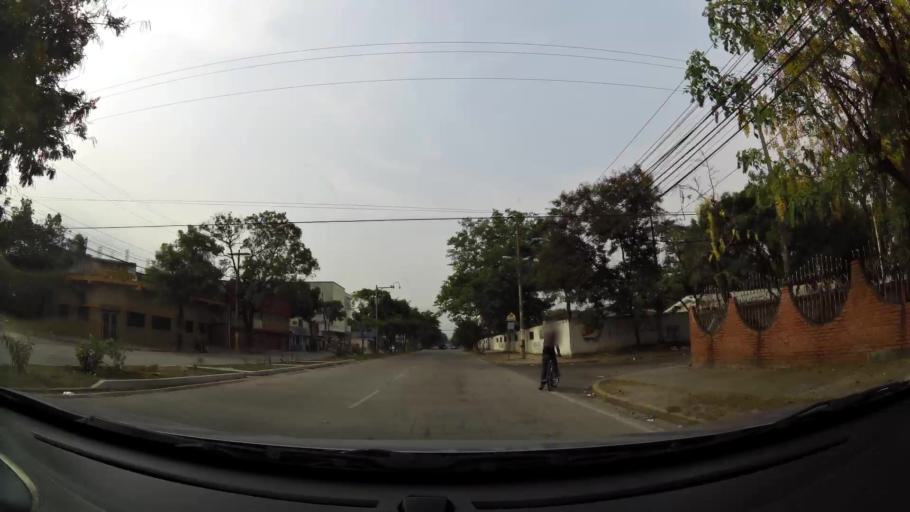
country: HN
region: Cortes
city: San Pedro Sula
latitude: 15.5120
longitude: -88.0183
